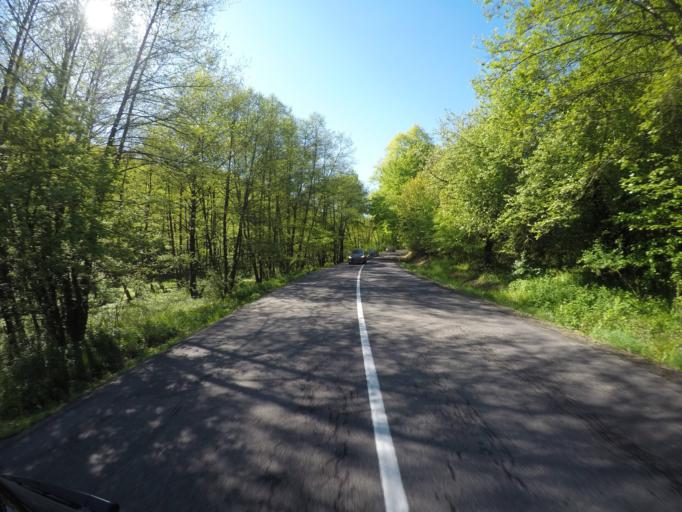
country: SK
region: Banskobystricky
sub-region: Okres Banska Bystrica
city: Banska Stiavnica
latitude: 48.5427
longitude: 19.0040
